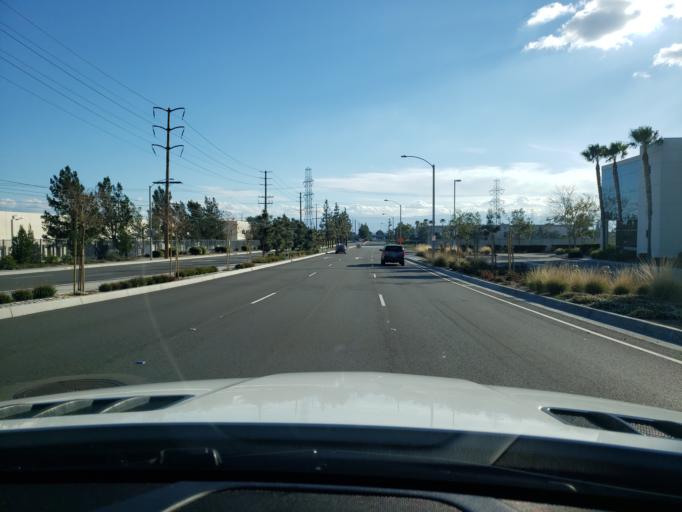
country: US
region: California
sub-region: Riverside County
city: Mira Loma
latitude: 34.0304
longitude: -117.5586
